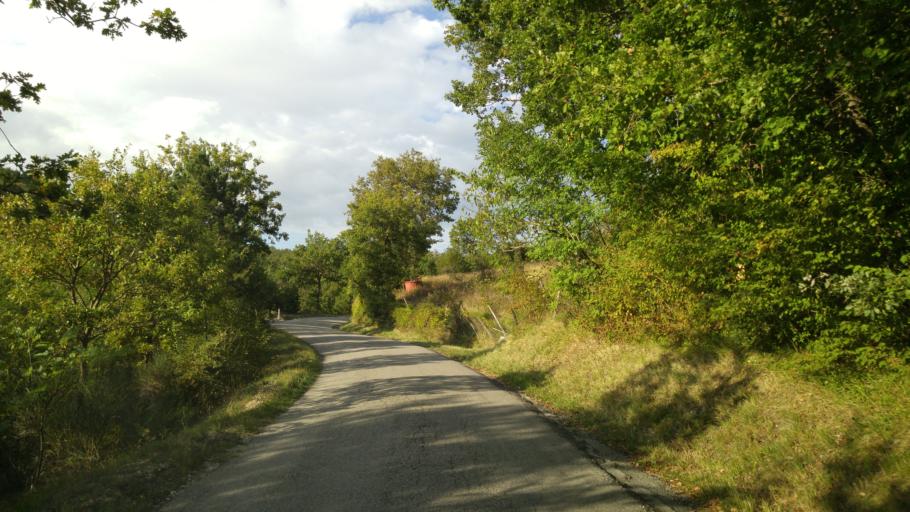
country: IT
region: The Marches
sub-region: Provincia di Pesaro e Urbino
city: Cagli
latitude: 43.5557
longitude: 12.6294
